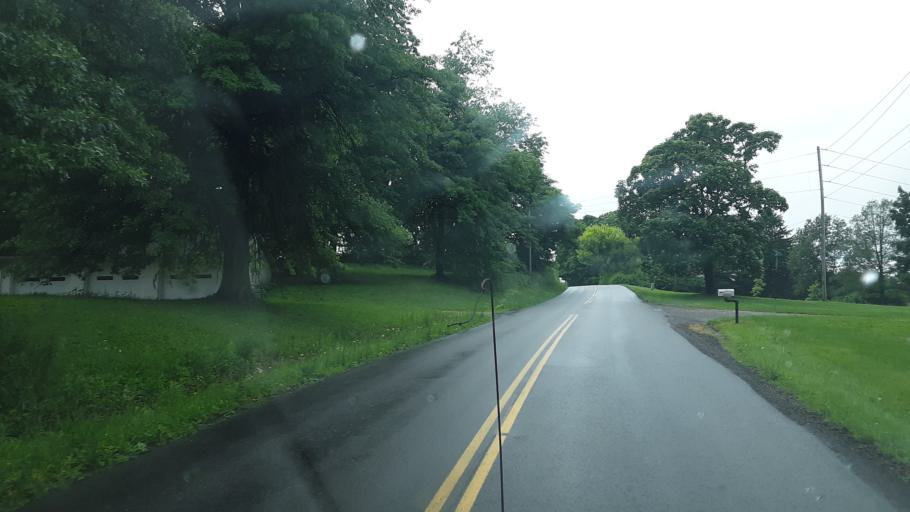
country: US
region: Ohio
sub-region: Carroll County
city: Carrollton
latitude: 40.6210
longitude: -81.0511
